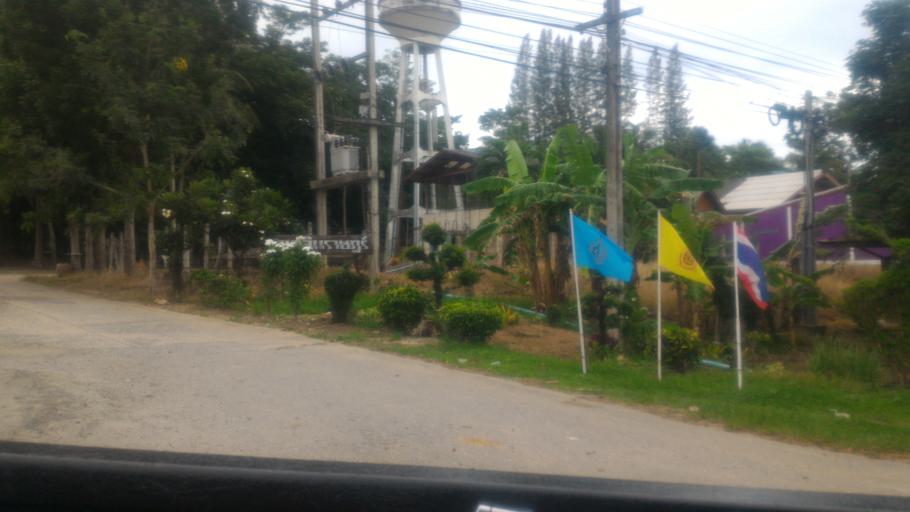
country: TH
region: Prachuap Khiri Khan
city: Kui Buri
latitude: 12.1069
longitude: 99.7533
